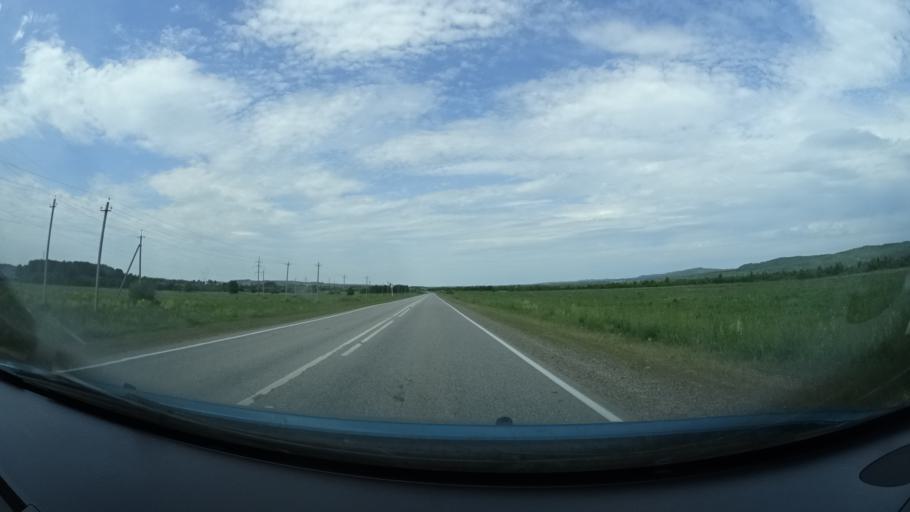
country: RU
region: Perm
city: Barda
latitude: 57.0736
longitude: 55.5425
